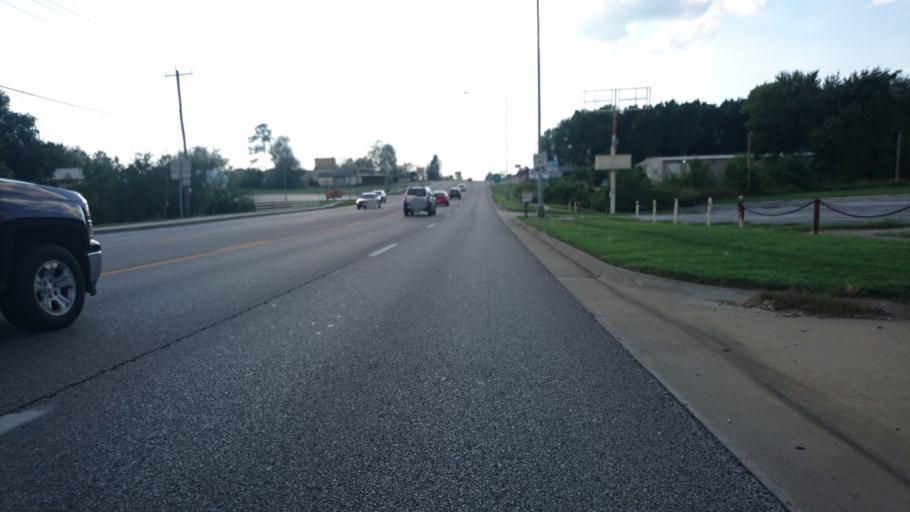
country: US
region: Missouri
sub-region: Greene County
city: Springfield
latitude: 37.2123
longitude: -93.3513
